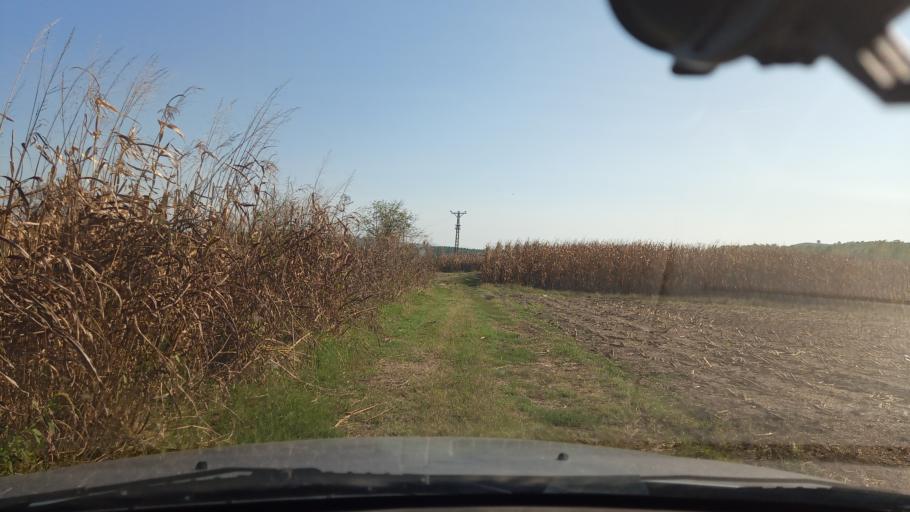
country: TR
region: Sakarya
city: Karasu
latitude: 41.0915
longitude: 30.5943
